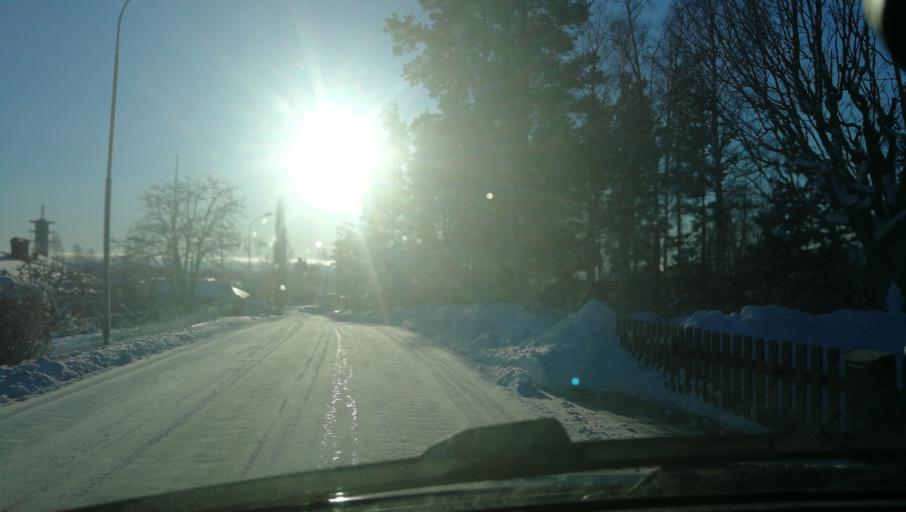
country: SE
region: Dalarna
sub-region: Mora Kommun
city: Mora
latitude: 60.9965
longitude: 14.5282
